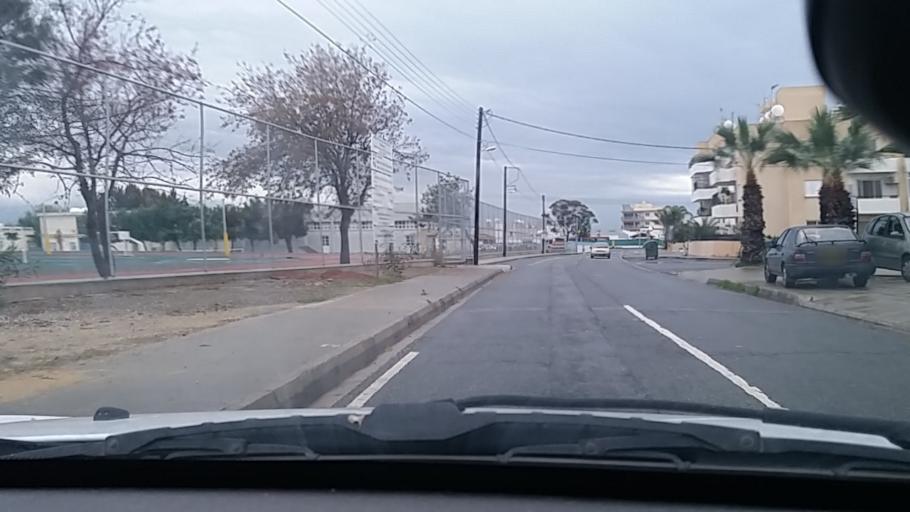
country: CY
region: Larnaka
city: Livadia
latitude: 34.9390
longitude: 33.6203
